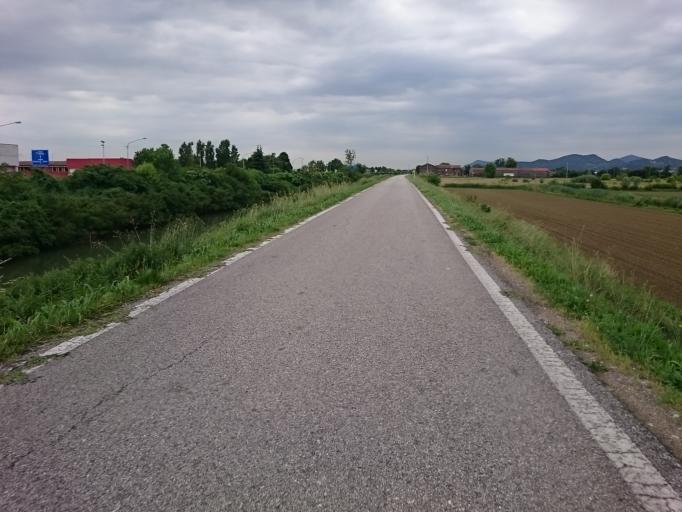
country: IT
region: Veneto
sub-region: Provincia di Padova
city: Mandriola-Sant'Agostino
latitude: 45.3564
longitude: 11.8363
